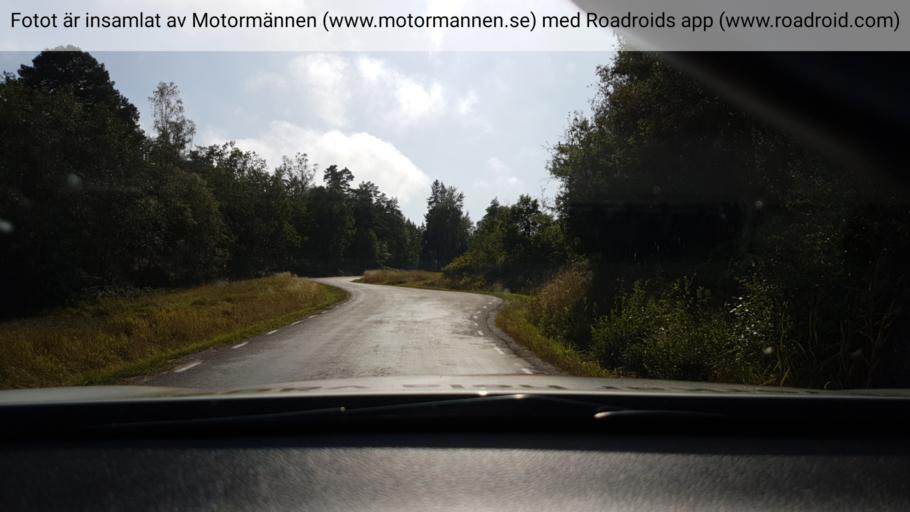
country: SE
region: Stockholm
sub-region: Nynashamns Kommun
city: Osmo
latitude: 58.8879
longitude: 17.7918
